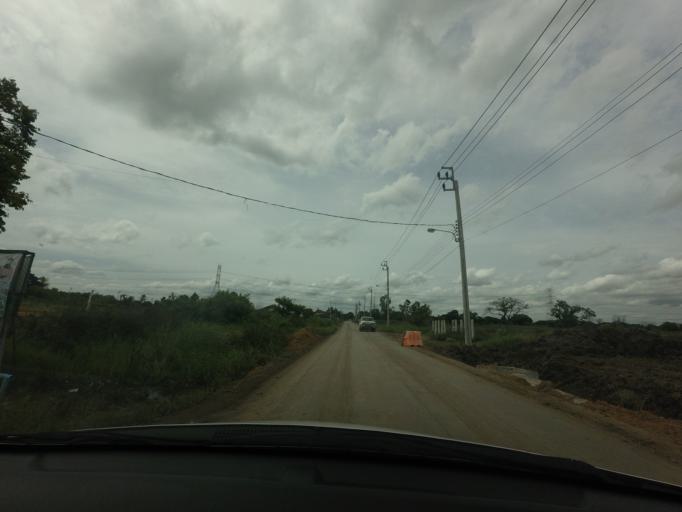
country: TH
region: Bangkok
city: Min Buri
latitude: 13.7837
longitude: 100.7613
